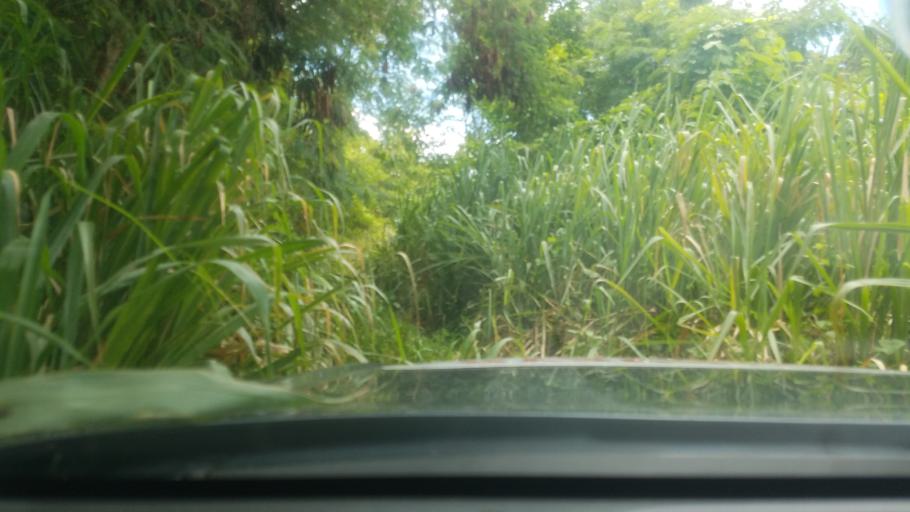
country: LC
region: Praslin
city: Praslin
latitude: 13.8801
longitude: -60.8985
